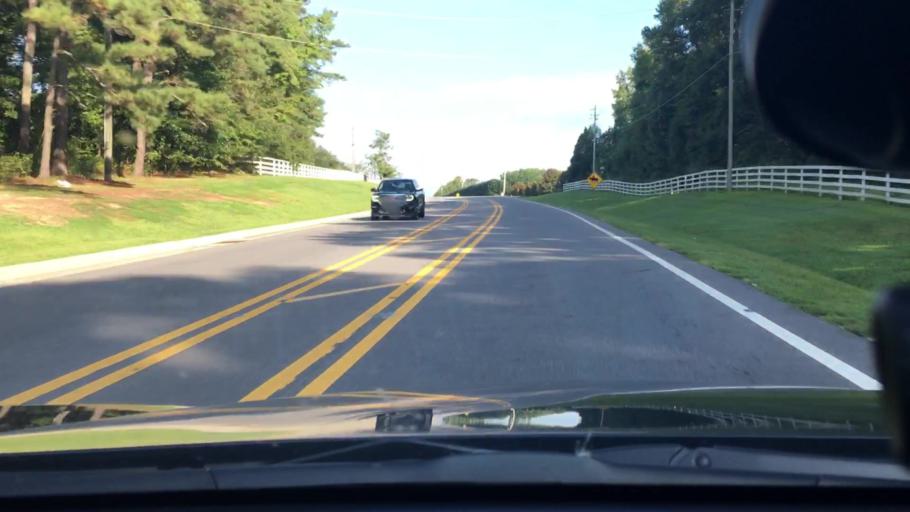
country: US
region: North Carolina
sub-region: Pitt County
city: Summerfield
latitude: 35.6432
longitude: -77.4560
